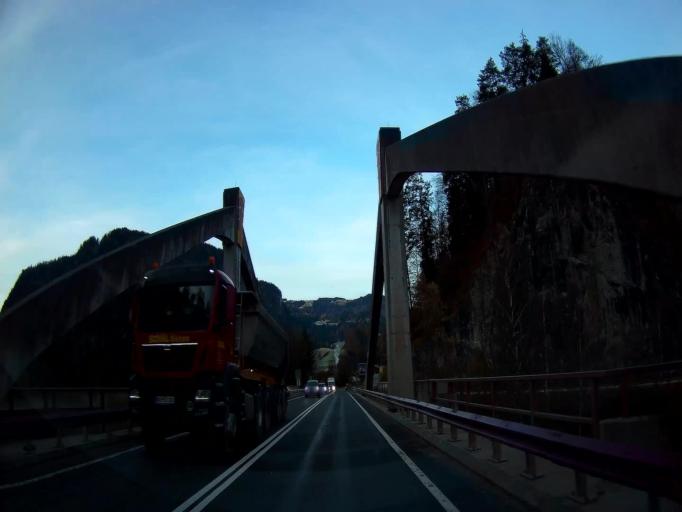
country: AT
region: Salzburg
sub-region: Politischer Bezirk Zell am See
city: Unken
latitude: 47.6483
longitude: 12.7353
